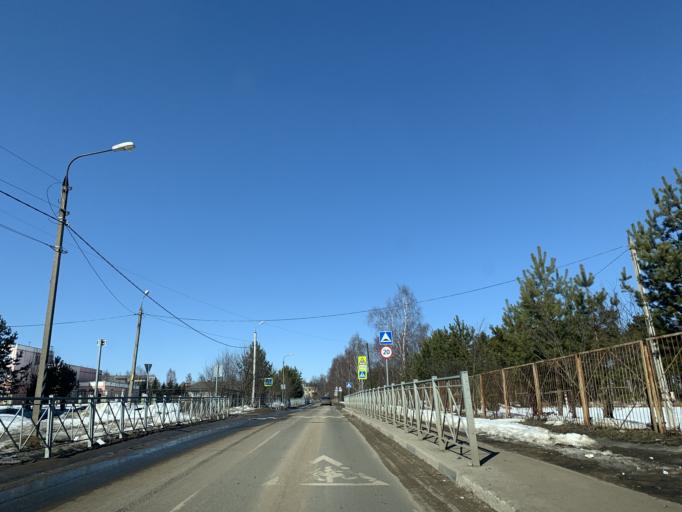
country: RU
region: Jaroslavl
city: Konstantinovskiy
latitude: 57.8388
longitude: 39.5829
